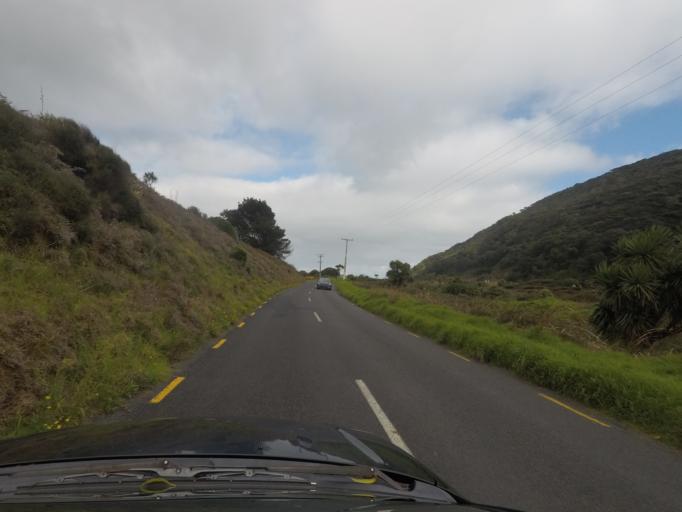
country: NZ
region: Auckland
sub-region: Auckland
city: Muriwai Beach
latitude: -36.8868
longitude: 174.4508
